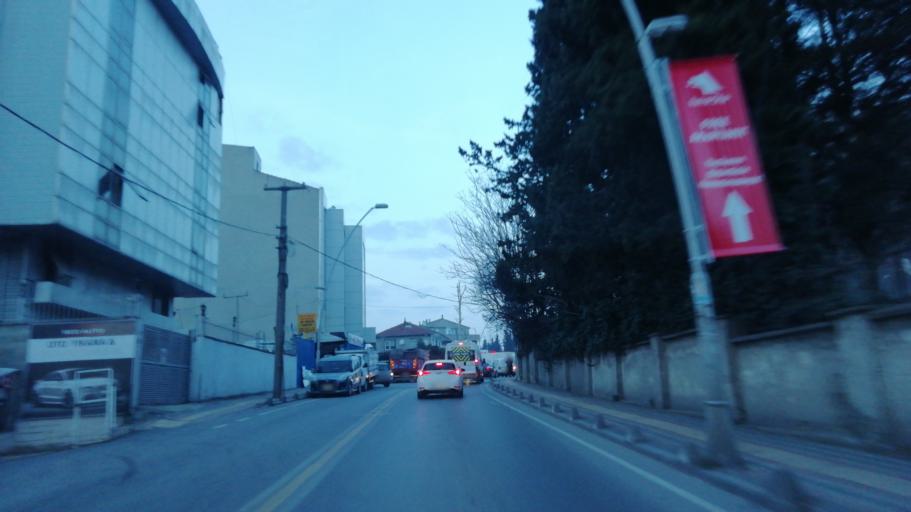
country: TR
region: Istanbul
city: Bahcelievler
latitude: 41.0102
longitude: 28.8228
